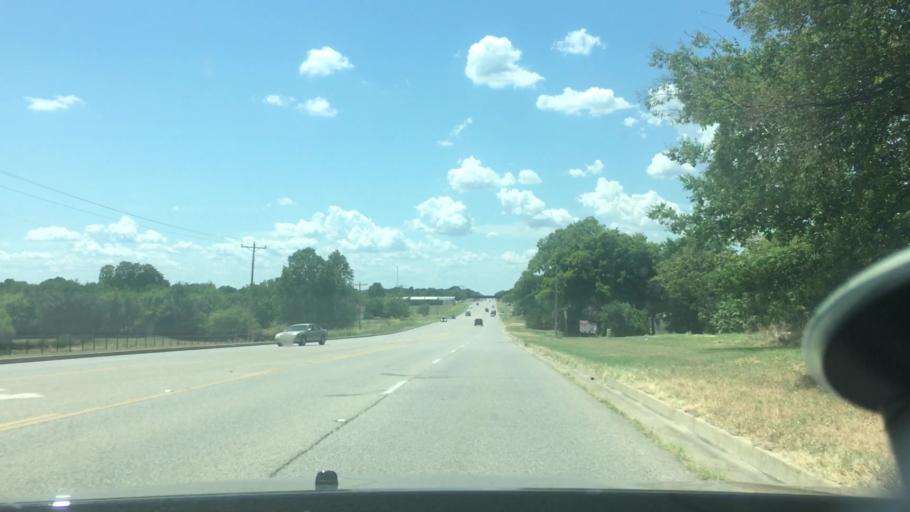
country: US
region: Oklahoma
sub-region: Bryan County
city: Calera
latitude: 33.9982
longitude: -96.5097
